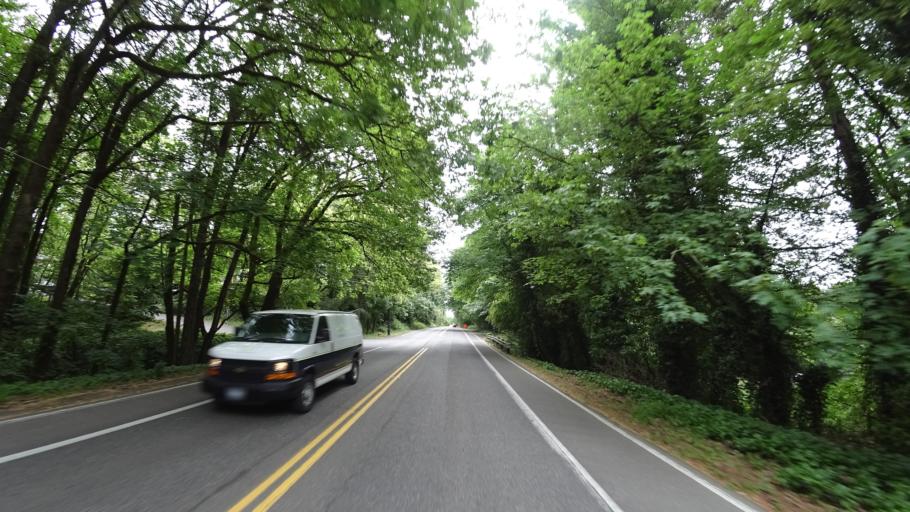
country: US
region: Oregon
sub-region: Washington County
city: Garden Home-Whitford
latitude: 45.4675
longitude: -122.7294
